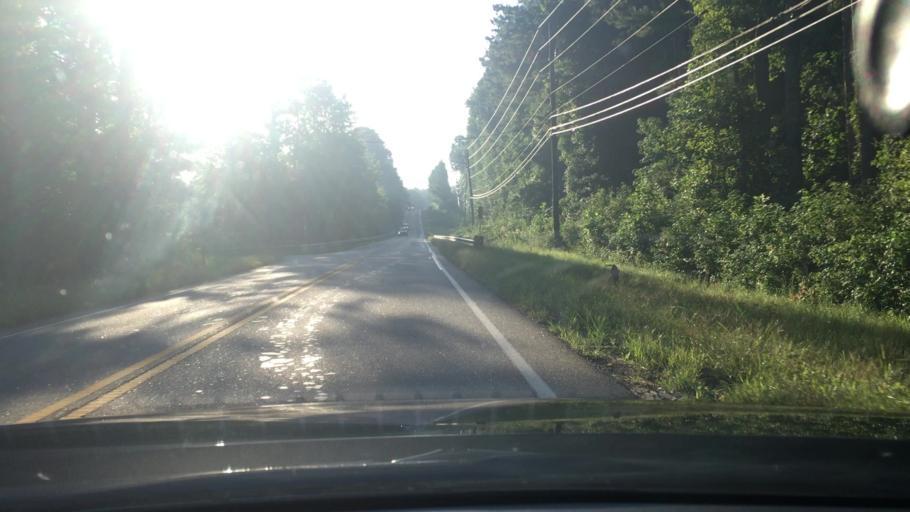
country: US
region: Georgia
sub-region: Coweta County
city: East Newnan
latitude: 33.3731
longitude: -84.7013
